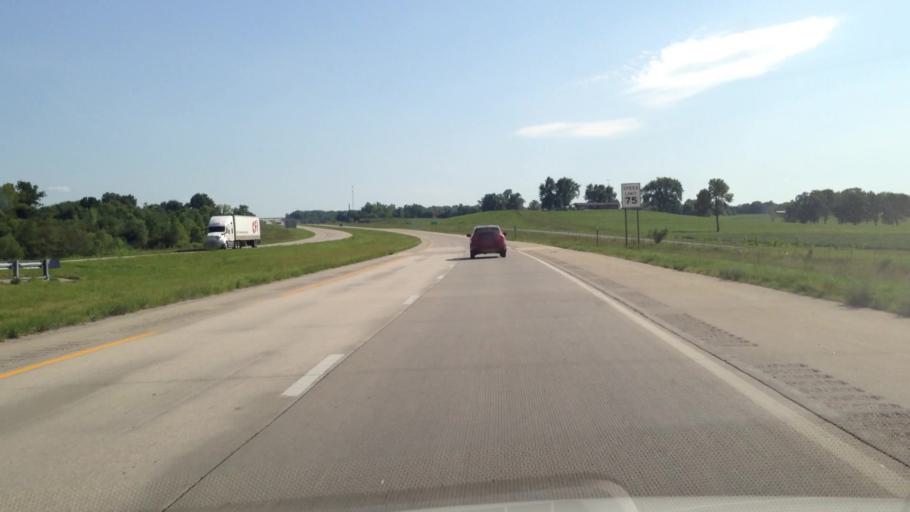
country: US
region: Kansas
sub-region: Linn County
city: Pleasanton
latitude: 38.1376
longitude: -94.7131
